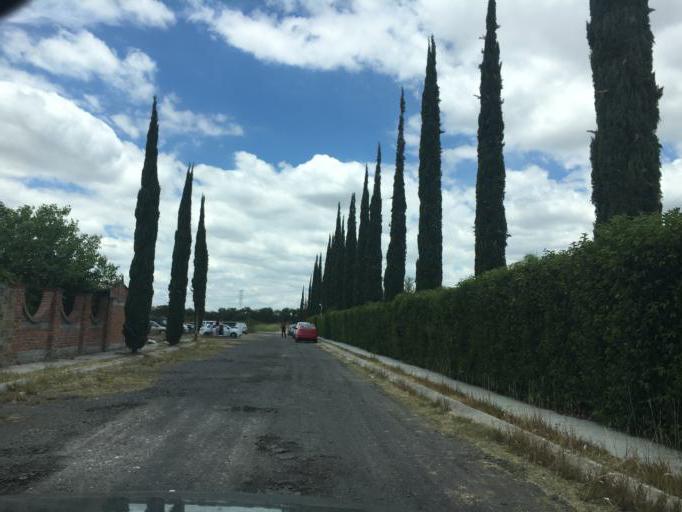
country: MX
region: Guanajuato
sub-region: San Francisco del Rincon
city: Barrio de Guadalupe del Mezquitillo
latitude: 20.9276
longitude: -101.7523
